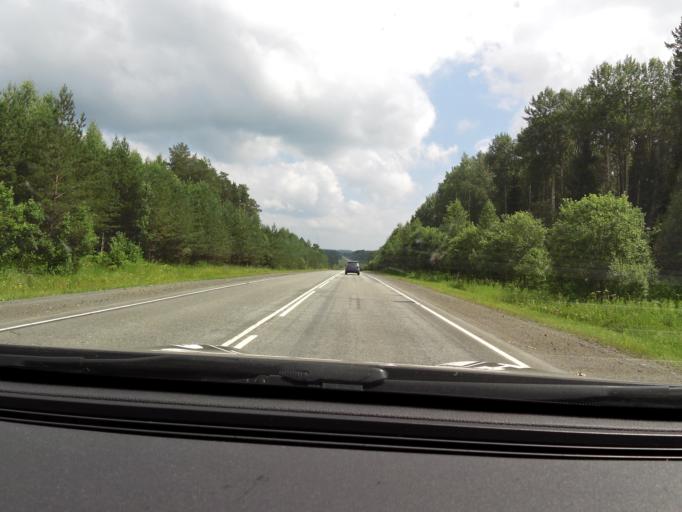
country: RU
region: Sverdlovsk
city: Achit
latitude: 56.8683
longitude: 57.6676
